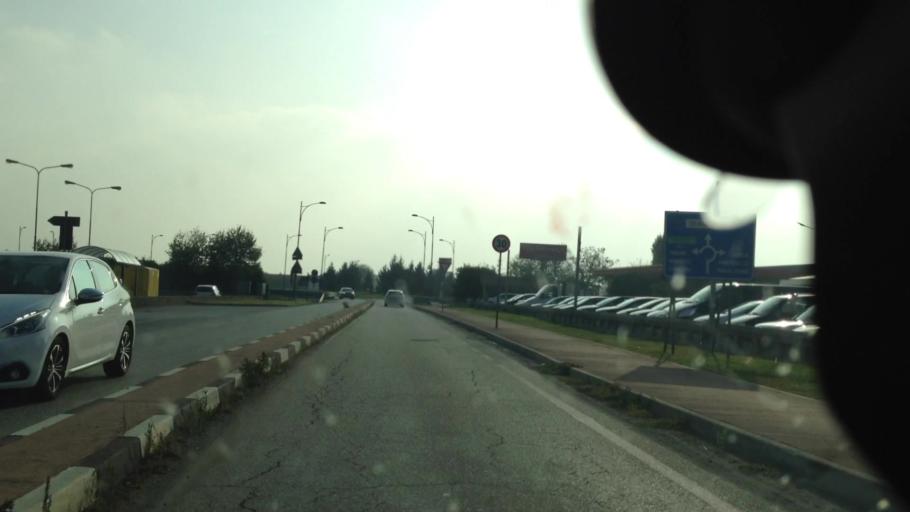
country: IT
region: Piedmont
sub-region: Provincia di Vercelli
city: Cigliano
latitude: 45.3187
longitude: 8.0305
